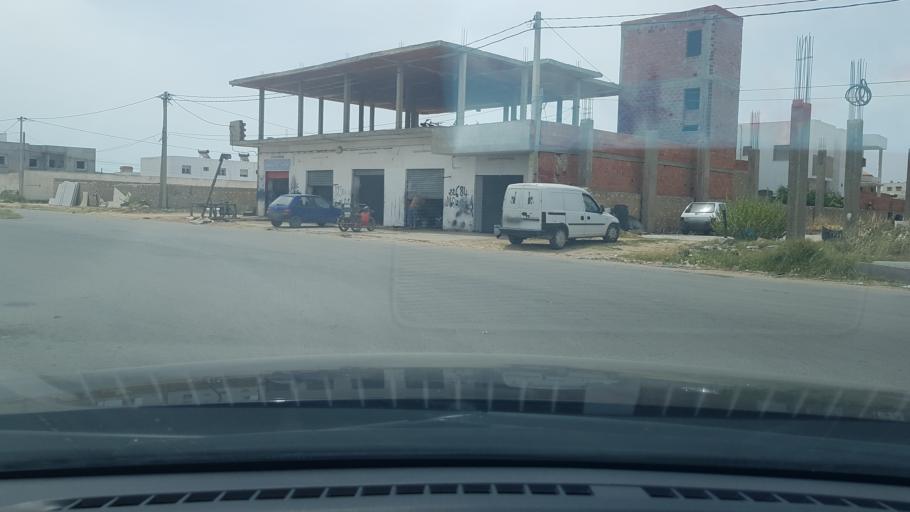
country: TN
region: Safaqis
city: Sfax
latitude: 34.8250
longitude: 10.7374
